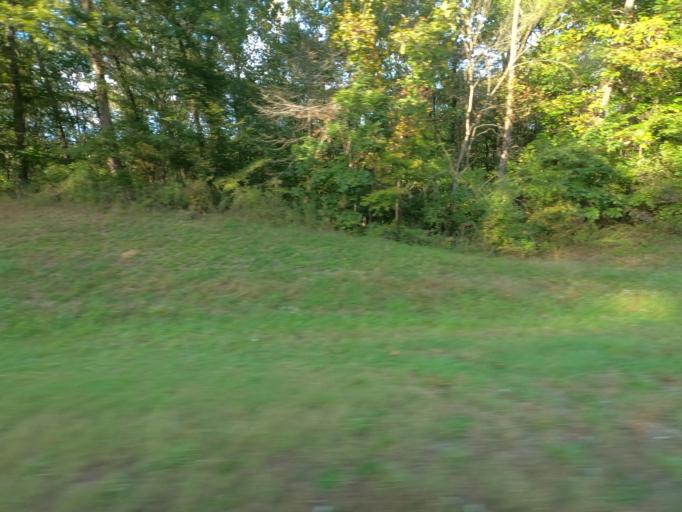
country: US
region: Tennessee
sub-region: Decatur County
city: Parsons
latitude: 35.8182
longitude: -88.2559
